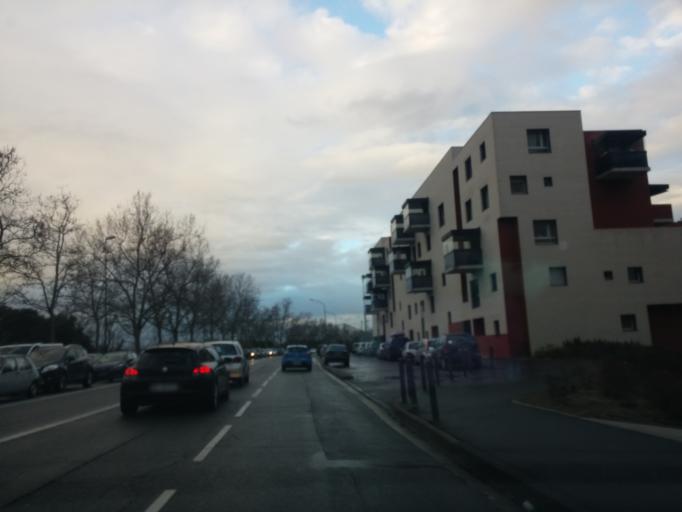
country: FR
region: Midi-Pyrenees
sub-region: Departement de la Haute-Garonne
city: Toulouse
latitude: 43.5774
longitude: 1.4366
